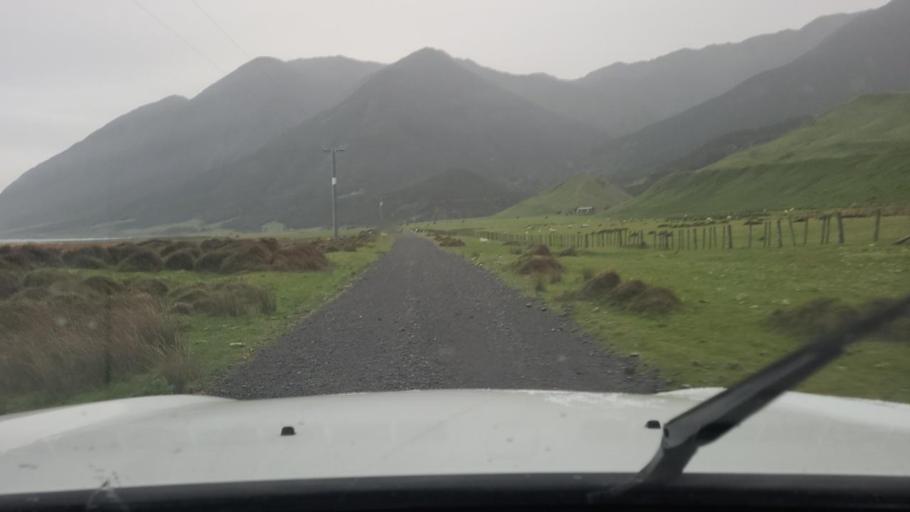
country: NZ
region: Wellington
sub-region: South Wairarapa District
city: Waipawa
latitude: -41.5680
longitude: 175.3778
